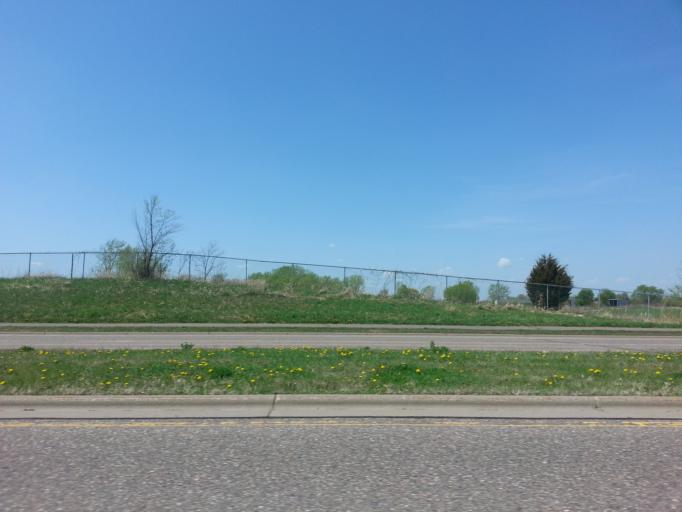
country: US
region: Minnesota
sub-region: Scott County
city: Savage
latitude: 44.7615
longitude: -93.3590
